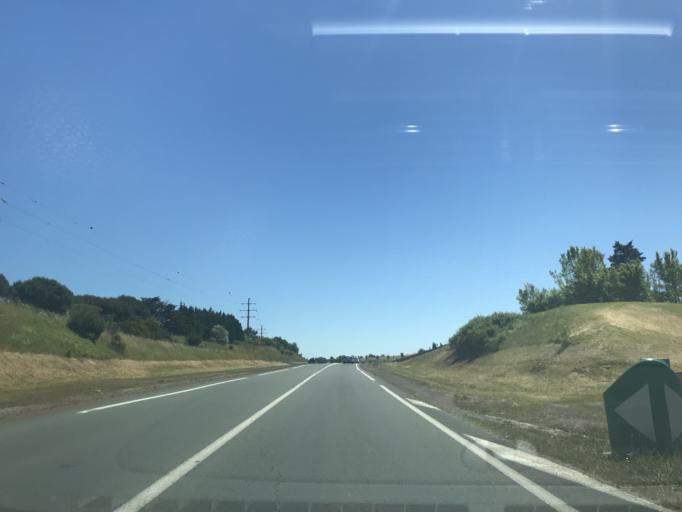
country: FR
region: Poitou-Charentes
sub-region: Departement de la Charente-Maritime
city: Saint-Georges-de-Didonne
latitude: 45.6256
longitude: -0.9989
